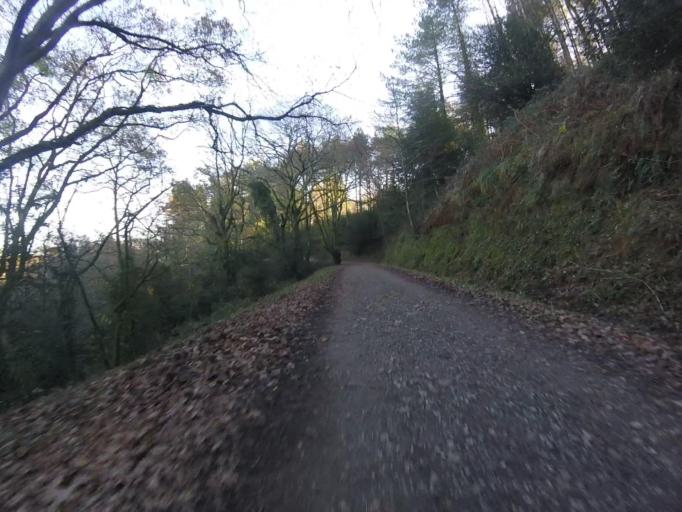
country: ES
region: Navarre
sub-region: Provincia de Navarra
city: Bera
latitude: 43.3187
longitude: -1.6941
